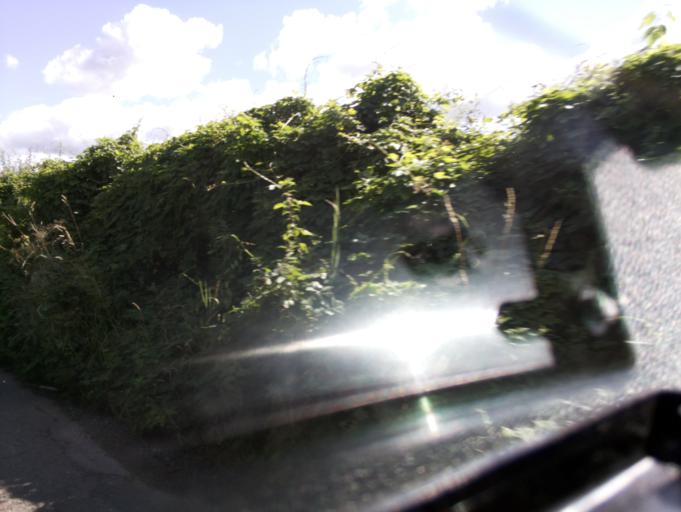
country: GB
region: England
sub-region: Gloucestershire
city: Gloucester
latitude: 51.8776
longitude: -2.3066
